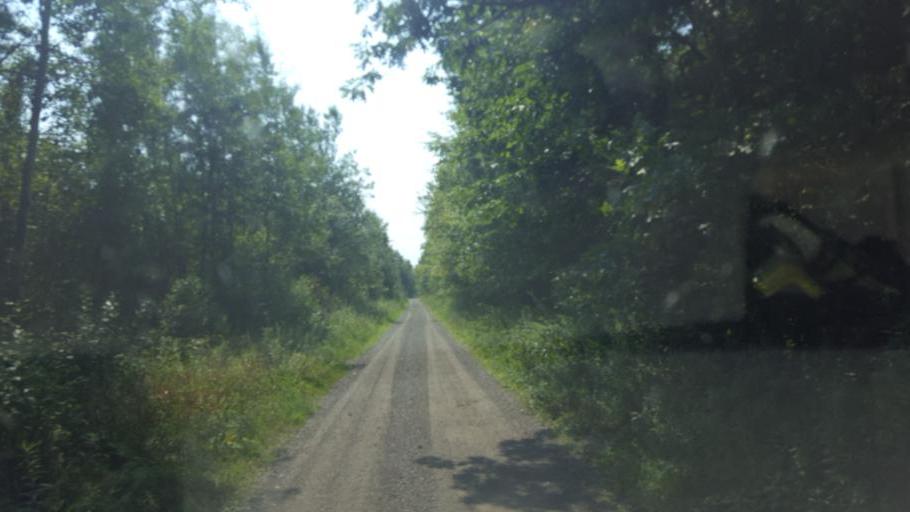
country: US
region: Ohio
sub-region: Ashtabula County
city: Orwell
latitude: 41.4778
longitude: -80.9047
